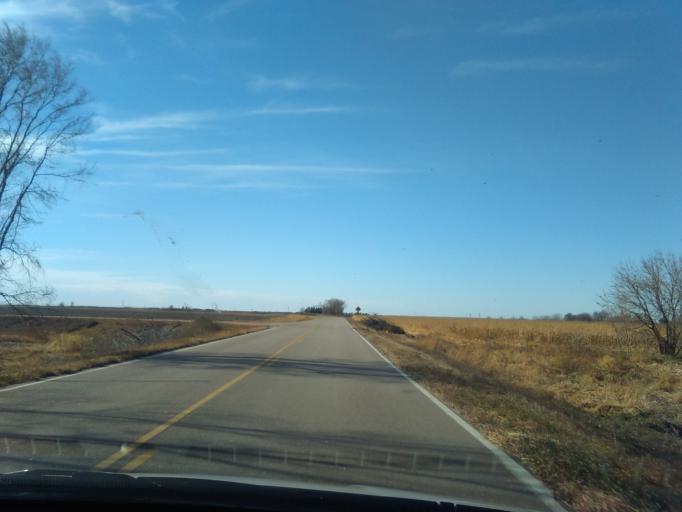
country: US
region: Nebraska
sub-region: Adams County
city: Hastings
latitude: 40.5100
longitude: -98.2479
